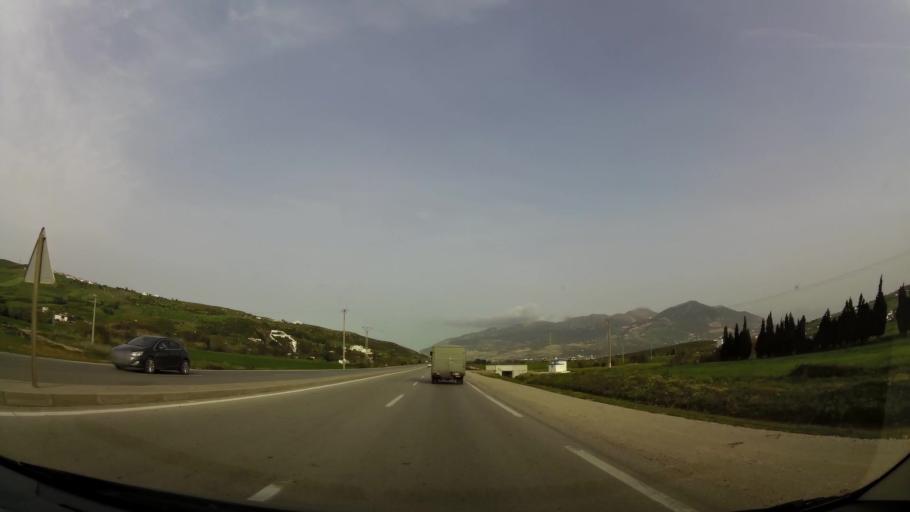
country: MA
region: Tanger-Tetouan
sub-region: Tetouan
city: Saddina
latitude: 35.5598
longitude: -5.4650
